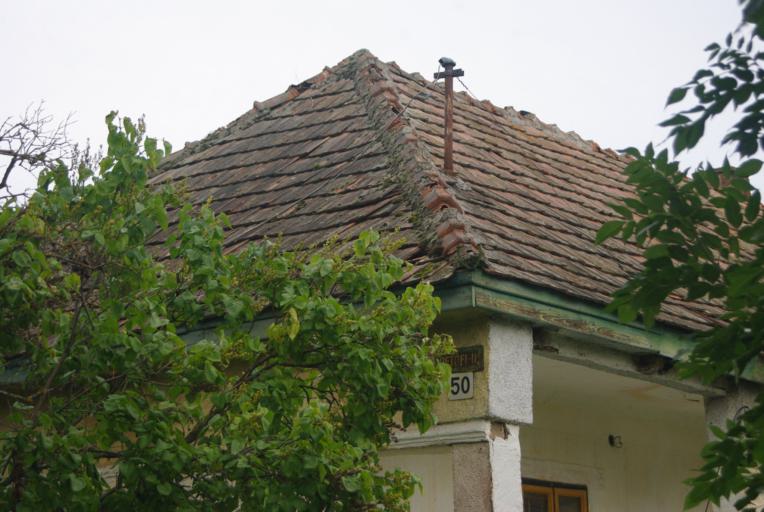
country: HU
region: Borsod-Abauj-Zemplen
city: Gonc
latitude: 48.3883
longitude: 21.2836
